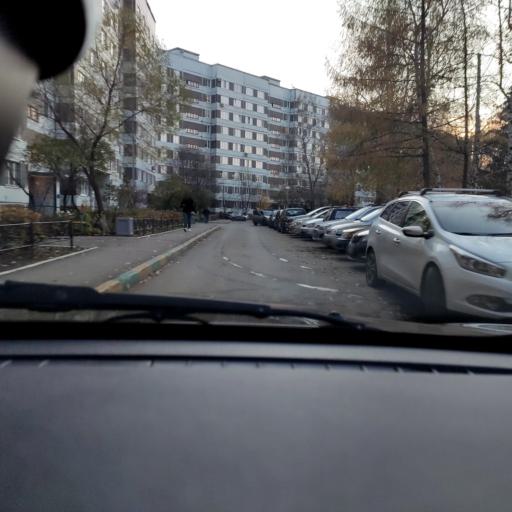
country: RU
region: Samara
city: Tol'yatti
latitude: 53.5299
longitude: 49.3366
